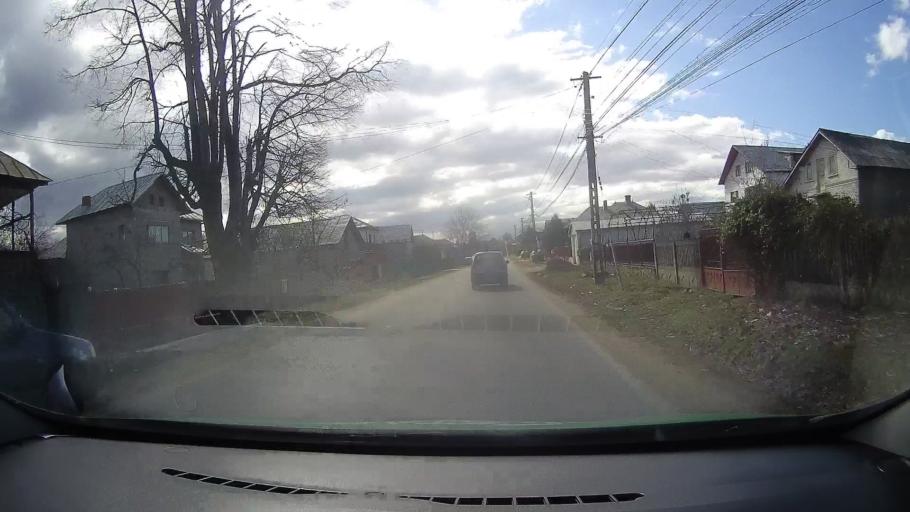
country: RO
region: Dambovita
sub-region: Comuna Branesti
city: Branesti
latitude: 45.0476
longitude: 25.4235
